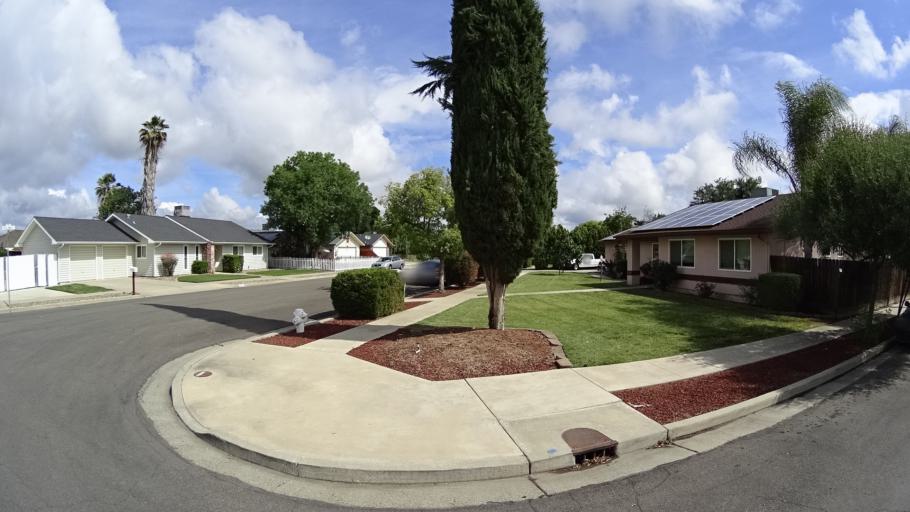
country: US
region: California
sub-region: Kings County
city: Hanford
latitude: 36.3455
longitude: -119.6613
